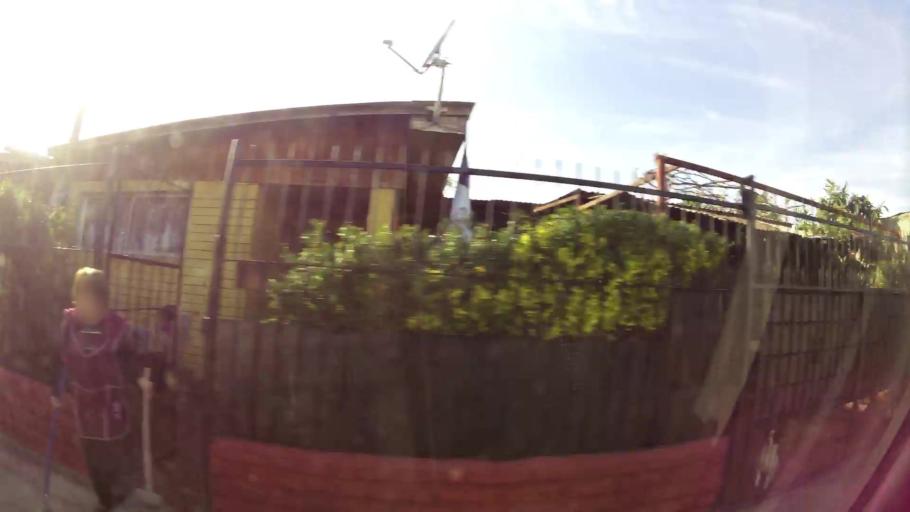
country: CL
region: Santiago Metropolitan
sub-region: Provincia de Talagante
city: Talagante
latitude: -33.6707
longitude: -70.9366
